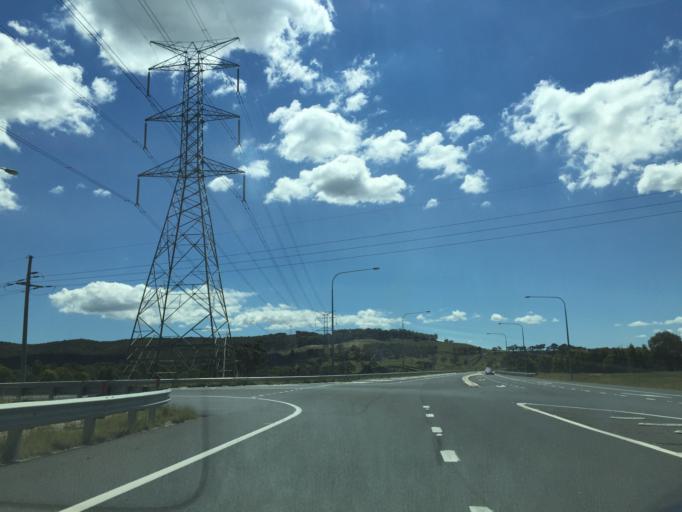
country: AU
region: New South Wales
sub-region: Lithgow
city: Lithgow
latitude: -33.3976
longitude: 150.0827
